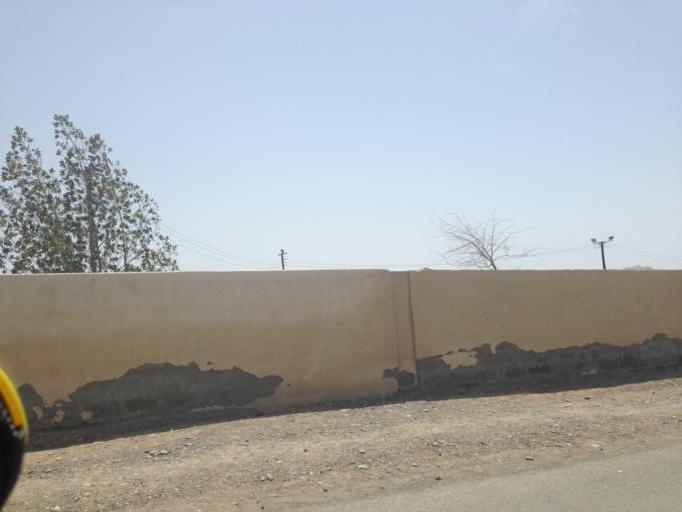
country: OM
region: Muhafazat Masqat
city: As Sib al Jadidah
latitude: 23.6850
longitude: 58.1178
